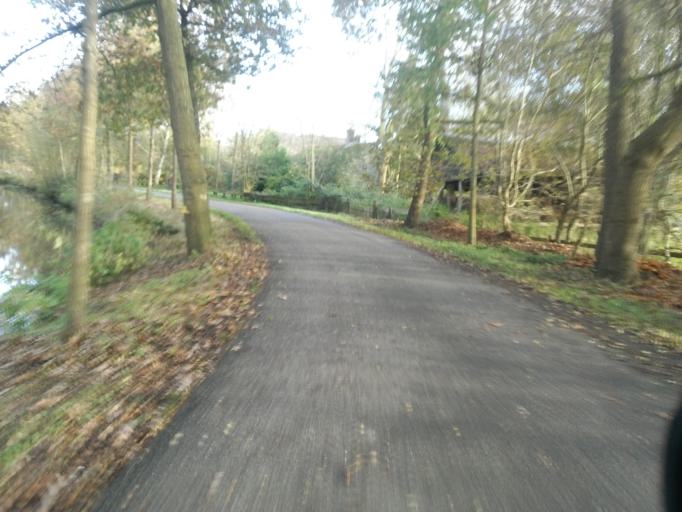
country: NL
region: Utrecht
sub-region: Gemeente Woudenberg
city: Woudenberg
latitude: 52.1031
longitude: 5.4068
